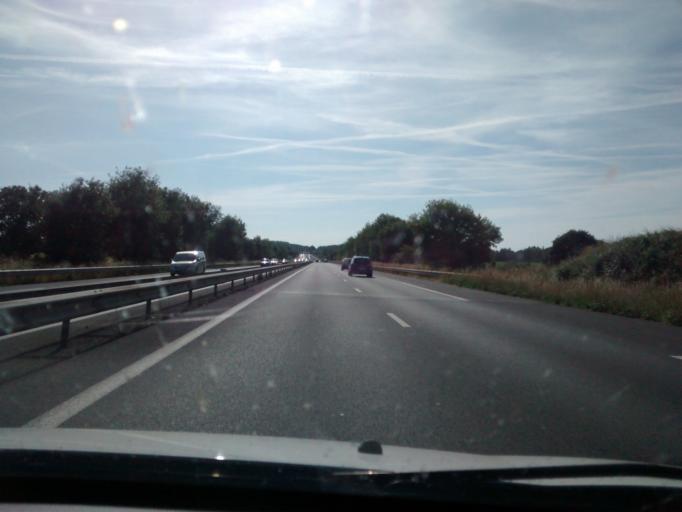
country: FR
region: Brittany
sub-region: Departement d'Ille-et-Vilaine
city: Torce
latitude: 48.0760
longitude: -1.2830
